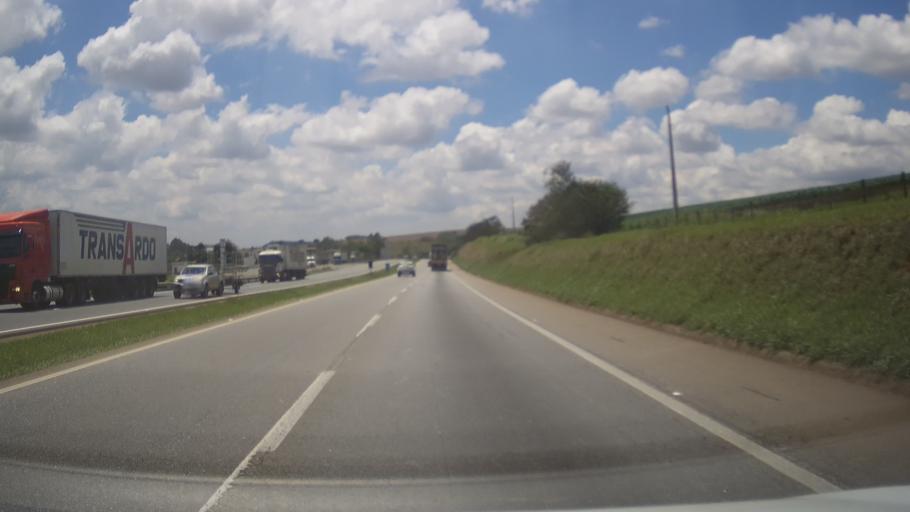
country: BR
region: Minas Gerais
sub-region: Campanha
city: Campanha
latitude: -21.7990
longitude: -45.4623
